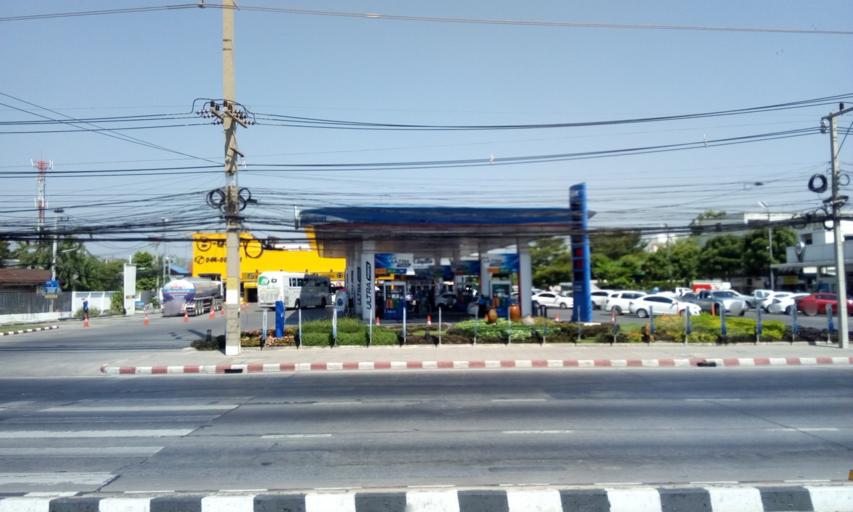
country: TH
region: Nakhon Ratchasima
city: Nakhon Ratchasima
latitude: 14.9796
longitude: 102.0814
